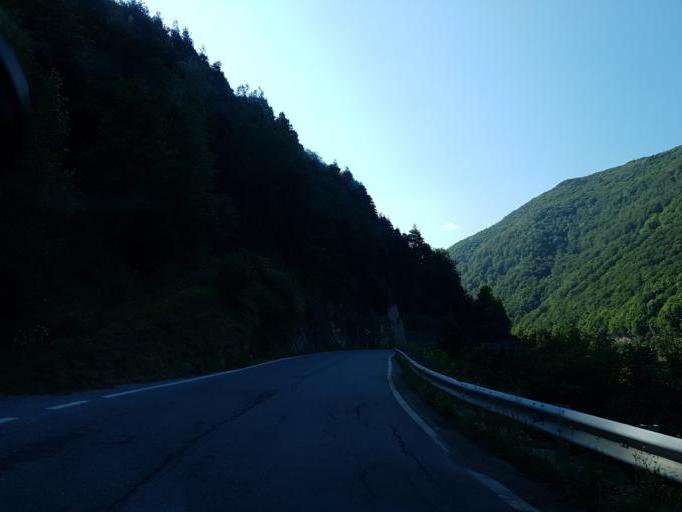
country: IT
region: Piedmont
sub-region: Provincia di Cuneo
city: San Damiano Macra
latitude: 44.4924
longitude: 7.2425
